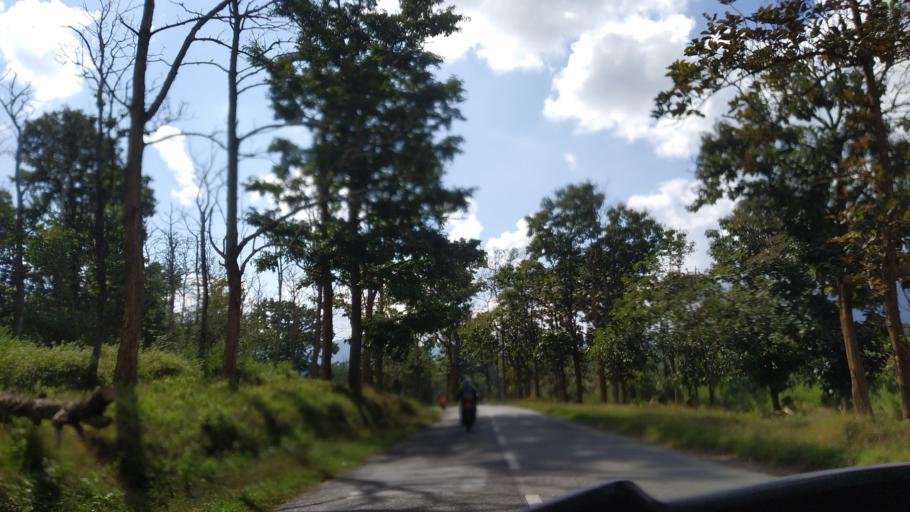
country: IN
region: Kerala
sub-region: Wayanad
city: Panamaram
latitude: 11.9189
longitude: 76.0662
